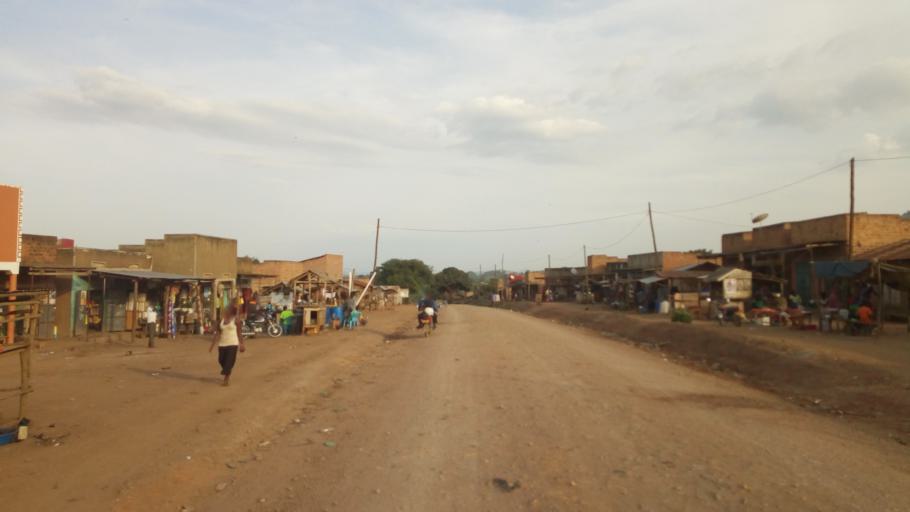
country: UG
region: Central Region
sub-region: Kiboga District
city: Kiboga
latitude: 0.7086
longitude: 31.7658
